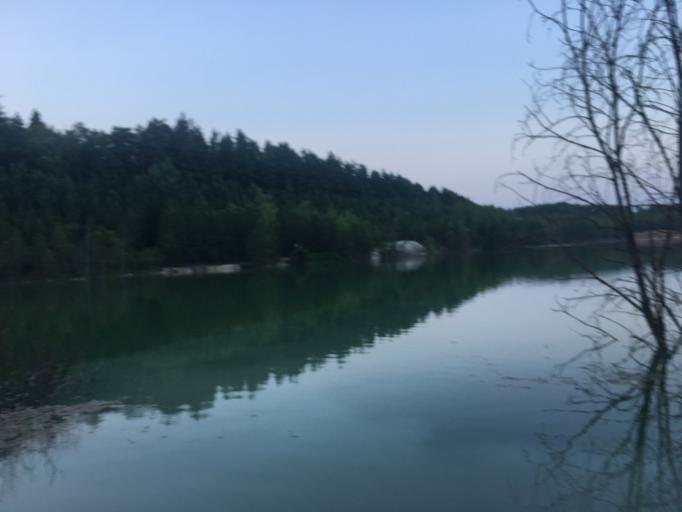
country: BY
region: Grodnenskaya
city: Hrodna
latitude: 53.7161
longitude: 23.7830
